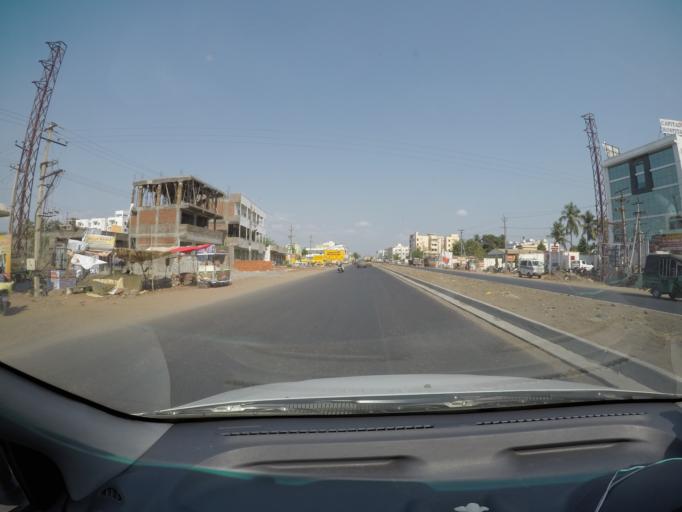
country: IN
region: Andhra Pradesh
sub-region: Krishna
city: Yanamalakuduru
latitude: 16.4783
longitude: 80.7015
